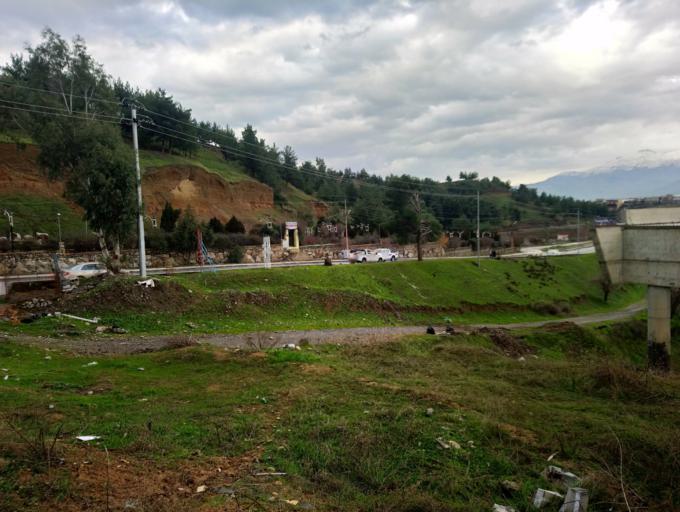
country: IQ
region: As Sulaymaniyah
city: Qeladize
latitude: 36.1856
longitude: 45.1123
